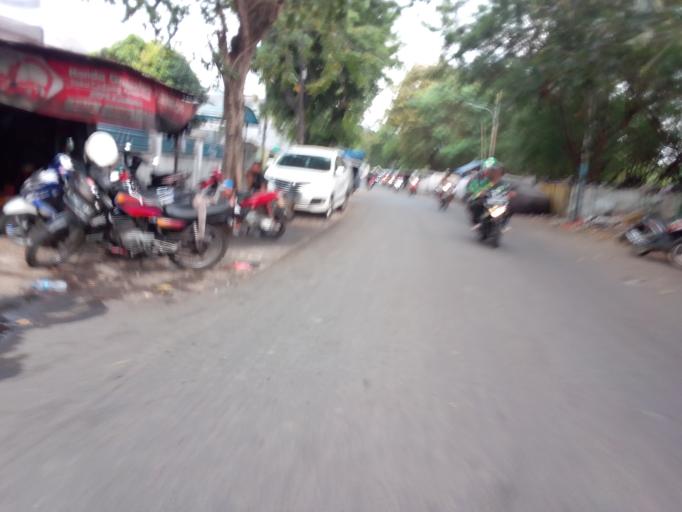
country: ID
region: Jakarta Raya
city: Jakarta
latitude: -6.1603
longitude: 106.8021
